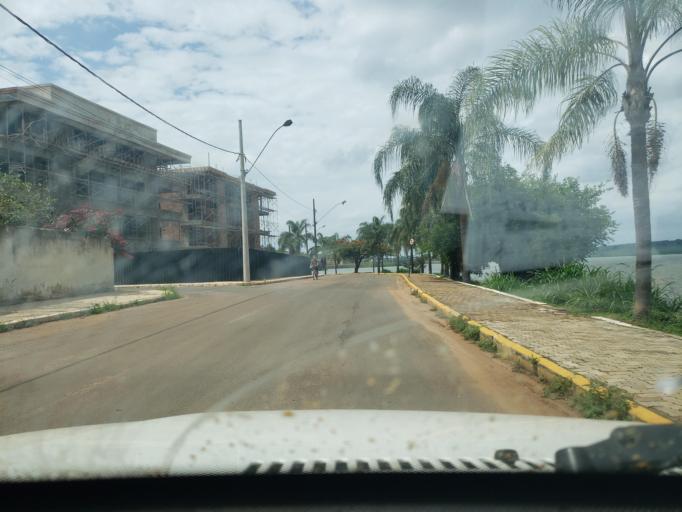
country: BR
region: Minas Gerais
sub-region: Boa Esperanca
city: Boa Esperanca
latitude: -21.0843
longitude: -45.5702
